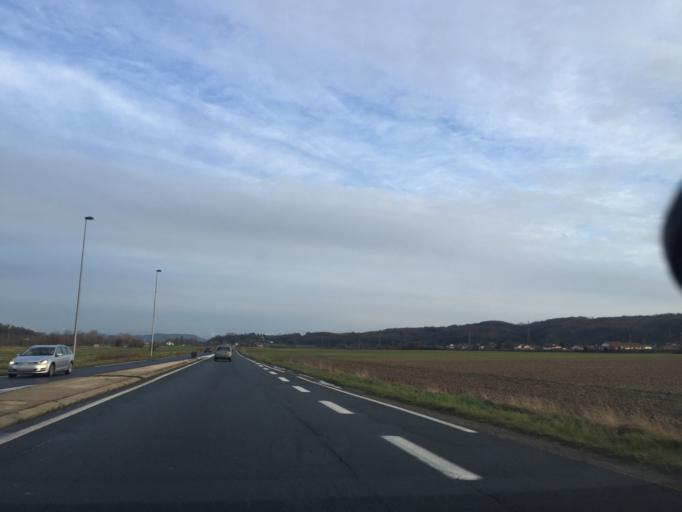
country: FR
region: Rhone-Alpes
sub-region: Departement de l'Isere
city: Vaulx-Milieu
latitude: 45.6178
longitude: 5.1850
